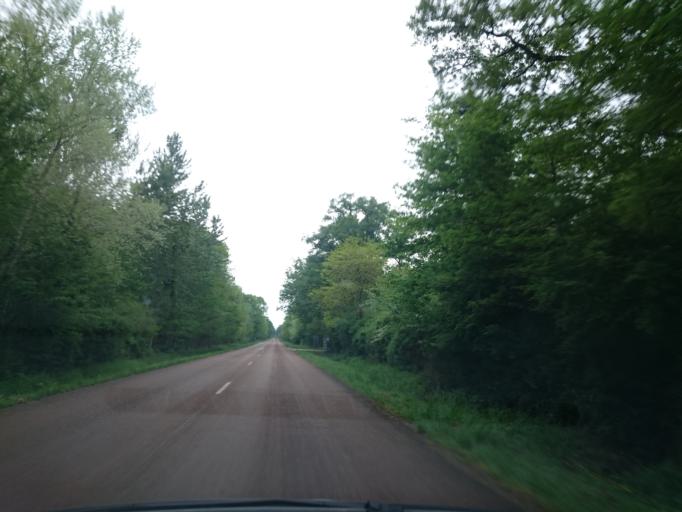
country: FR
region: Centre
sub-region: Departement du Loir-et-Cher
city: Muides-sur-Loire
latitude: 47.6469
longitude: 1.5270
